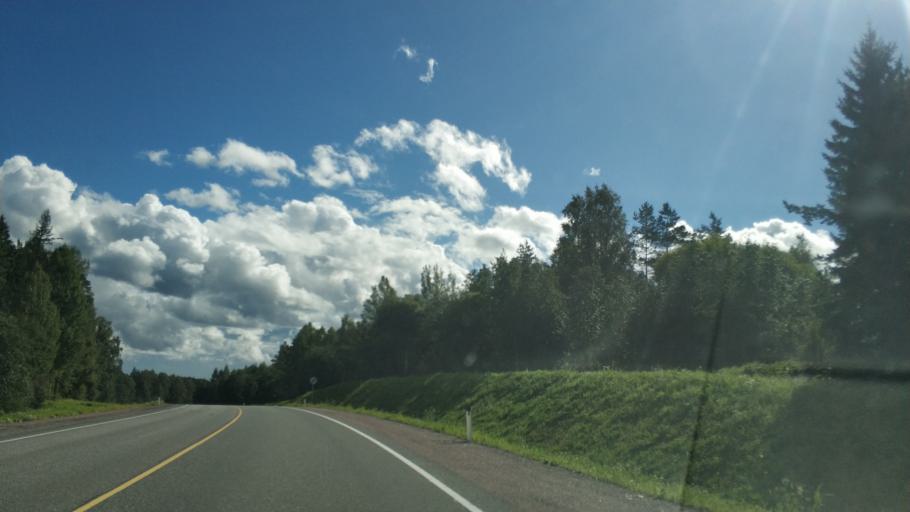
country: RU
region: Republic of Karelia
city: Ruskeala
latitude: 61.8959
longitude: 30.6375
